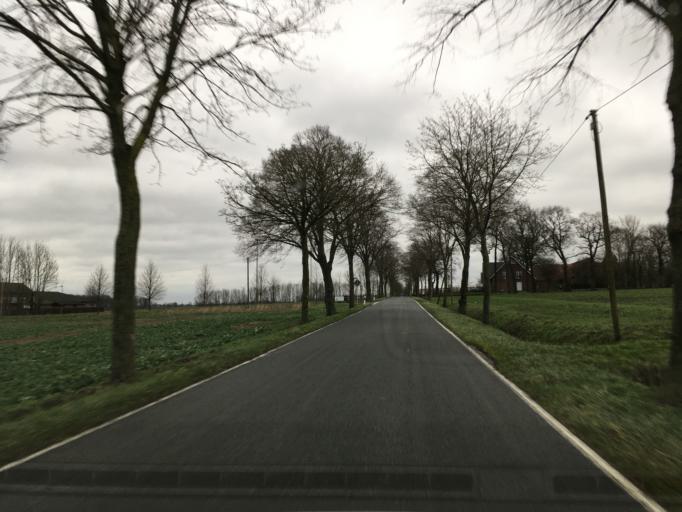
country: DE
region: North Rhine-Westphalia
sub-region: Regierungsbezirk Munster
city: Legden
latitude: 52.0679
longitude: 7.1565
